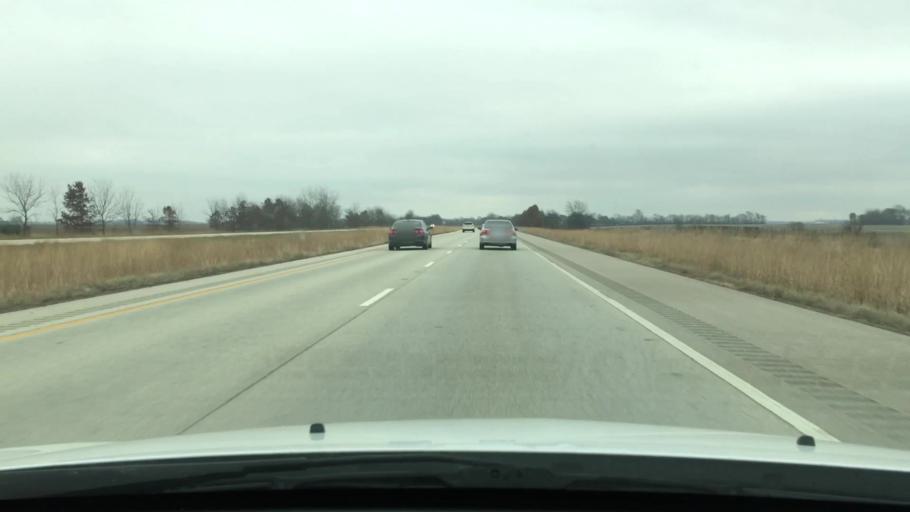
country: US
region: Illinois
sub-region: Sangamon County
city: New Berlin
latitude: 39.7410
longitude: -89.8405
